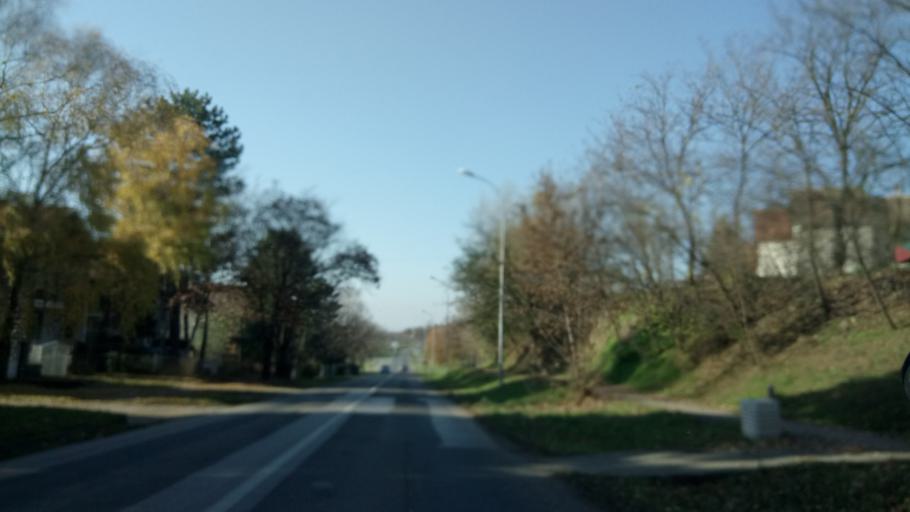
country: RS
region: Autonomna Pokrajina Vojvodina
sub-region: Sremski Okrug
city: Ingija
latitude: 45.0535
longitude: 20.0702
